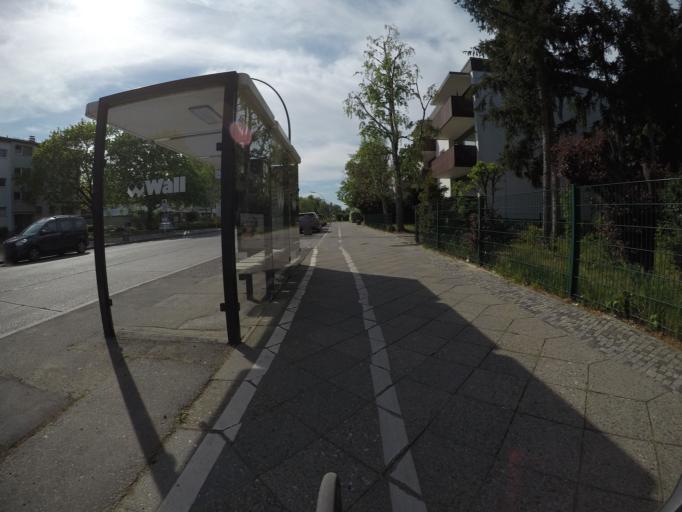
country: DE
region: Berlin
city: Lankwitz
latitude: 52.4151
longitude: 13.3463
